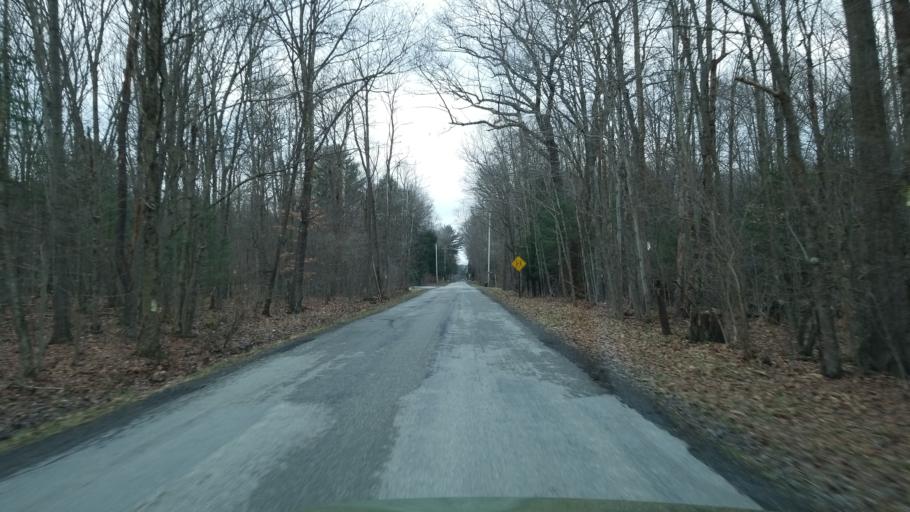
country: US
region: Pennsylvania
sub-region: Jefferson County
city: Falls Creek
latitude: 41.1818
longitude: -78.7972
